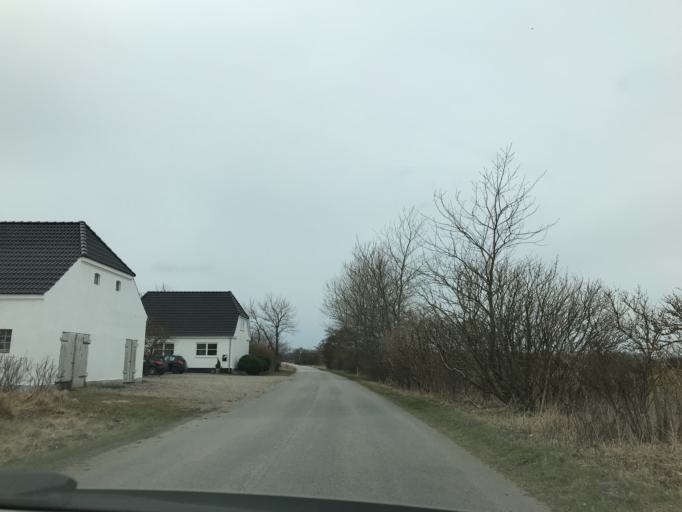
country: DK
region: South Denmark
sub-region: Varde Kommune
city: Oksbol
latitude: 55.8042
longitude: 8.3548
